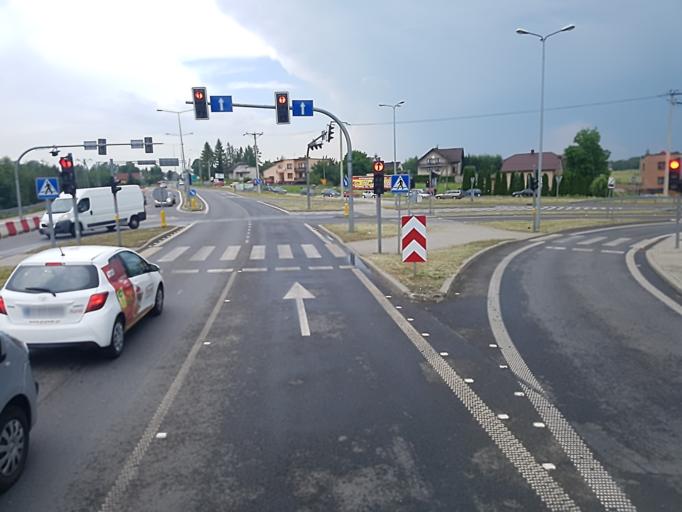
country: PL
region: Silesian Voivodeship
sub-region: Powiat wodzislawski
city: Mszana
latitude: 49.9735
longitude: 18.5338
